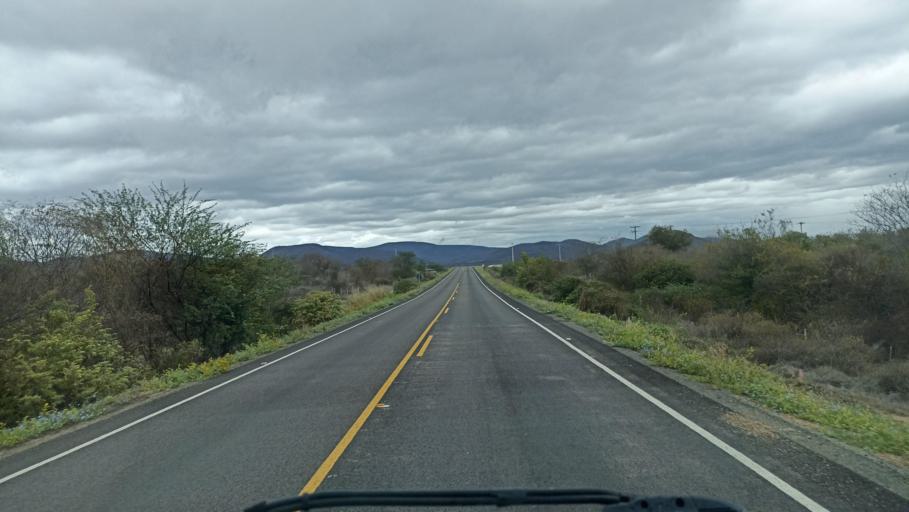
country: BR
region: Bahia
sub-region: Iacu
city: Iacu
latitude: -12.9132
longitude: -40.4100
